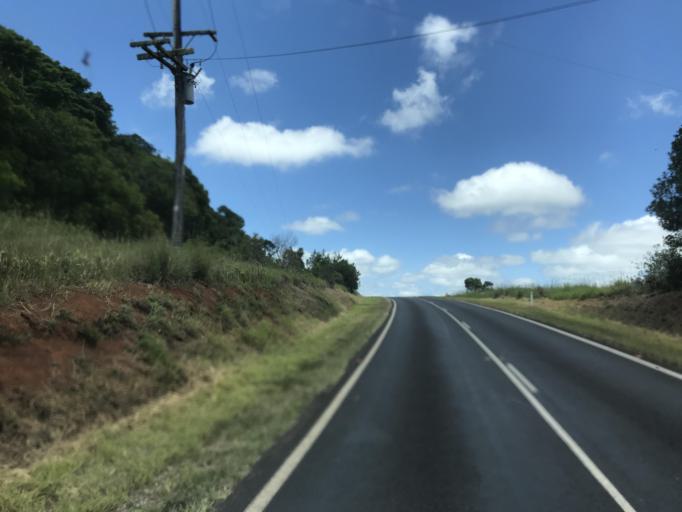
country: AU
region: Queensland
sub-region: Tablelands
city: Ravenshoe
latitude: -17.4984
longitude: 145.4768
